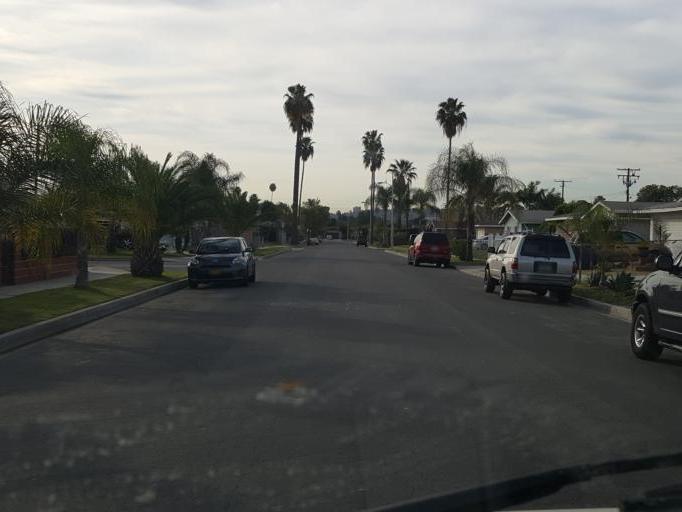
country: US
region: California
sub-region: Los Angeles County
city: West Puente Valley
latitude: 34.0508
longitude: -117.9653
